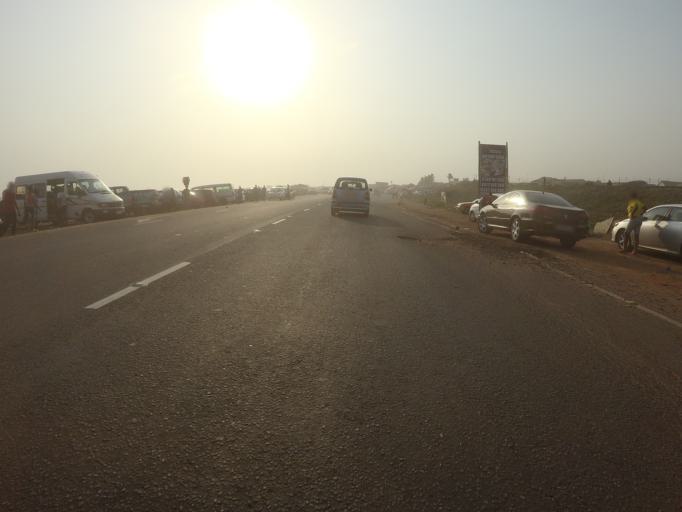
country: GH
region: Greater Accra
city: Nungua
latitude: 5.6119
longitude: -0.0438
